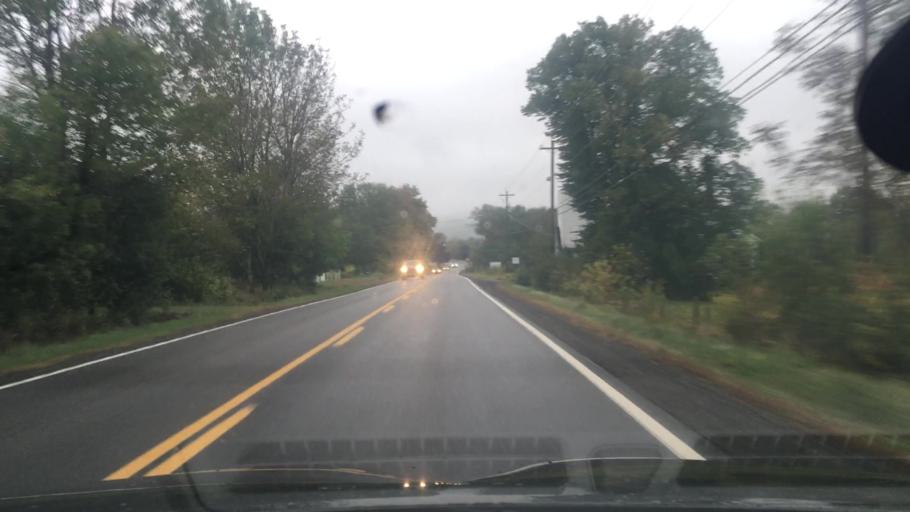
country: CA
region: Nova Scotia
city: Windsor
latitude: 44.9444
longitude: -64.1826
